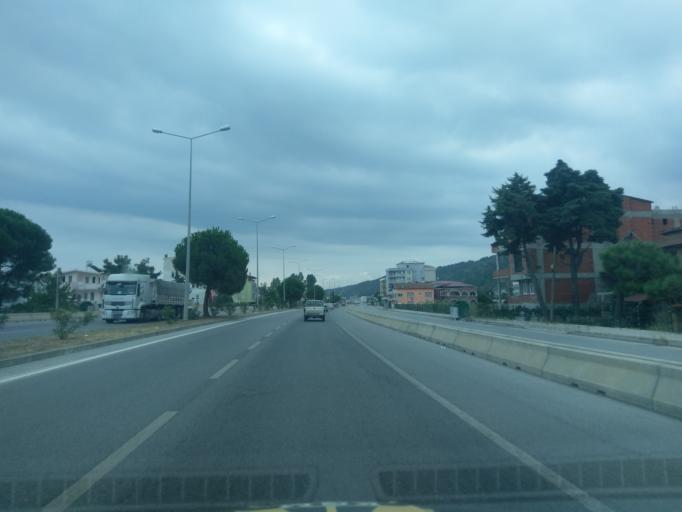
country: TR
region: Samsun
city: Taflan
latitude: 41.3957
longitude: 36.1978
